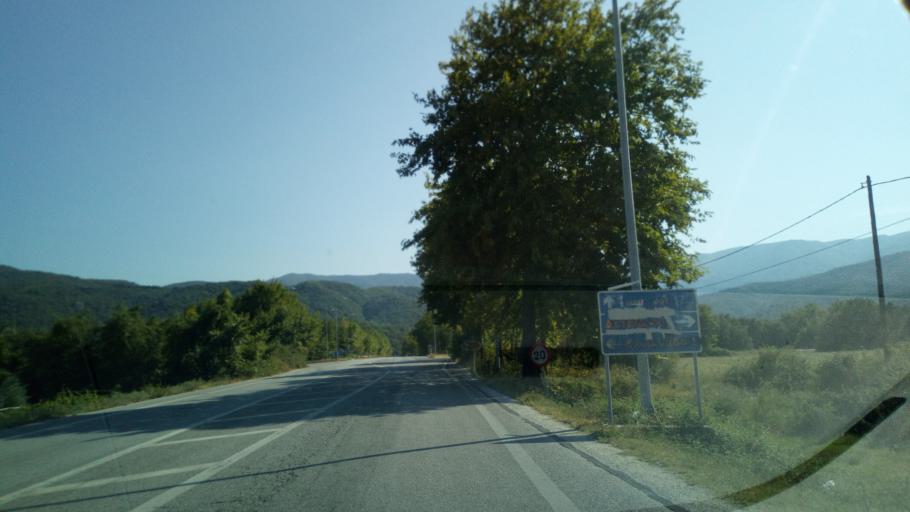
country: GR
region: Central Macedonia
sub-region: Nomos Thessalonikis
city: Stavros
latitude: 40.5955
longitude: 23.7686
